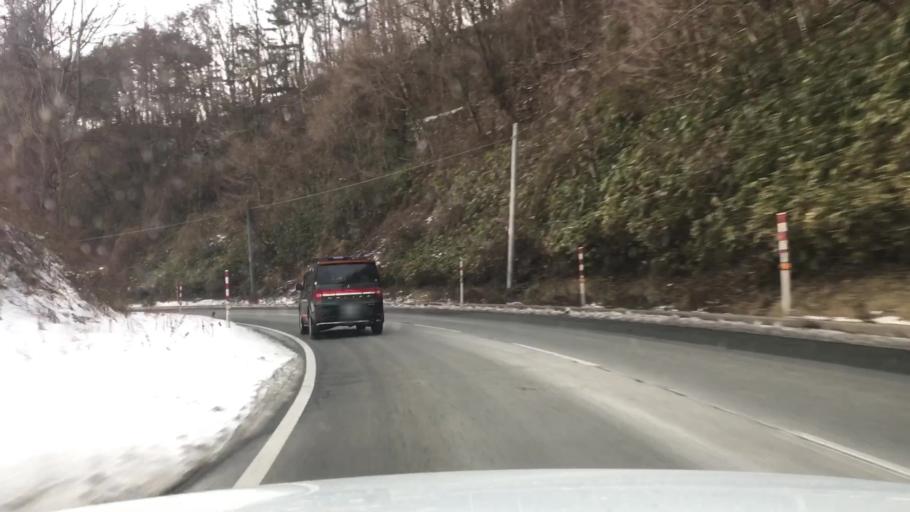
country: JP
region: Iwate
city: Morioka-shi
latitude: 39.6714
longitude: 141.3332
